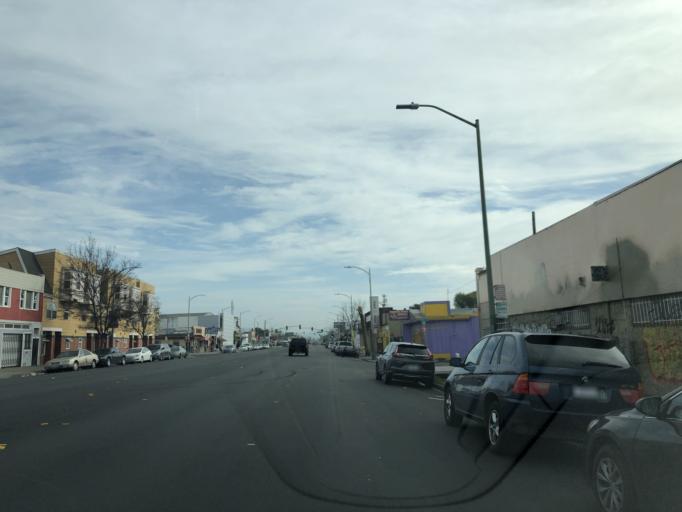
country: US
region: California
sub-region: Alameda County
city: Alameda
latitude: 37.7649
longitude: -122.1993
